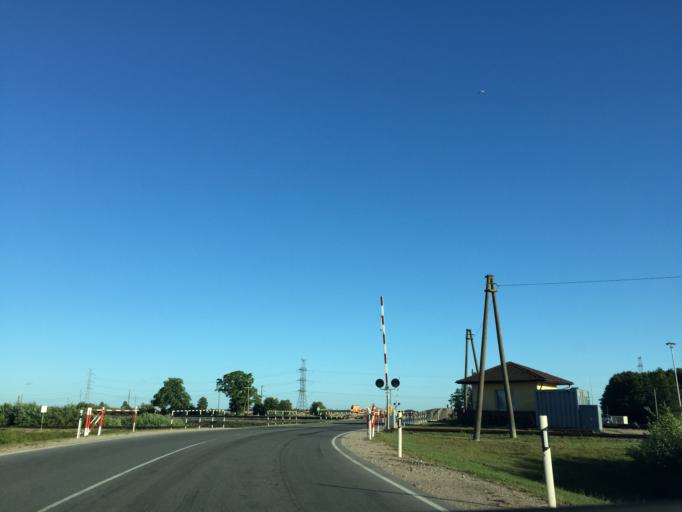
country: LV
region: Ventspils
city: Ventspils
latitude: 57.3938
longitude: 21.6375
